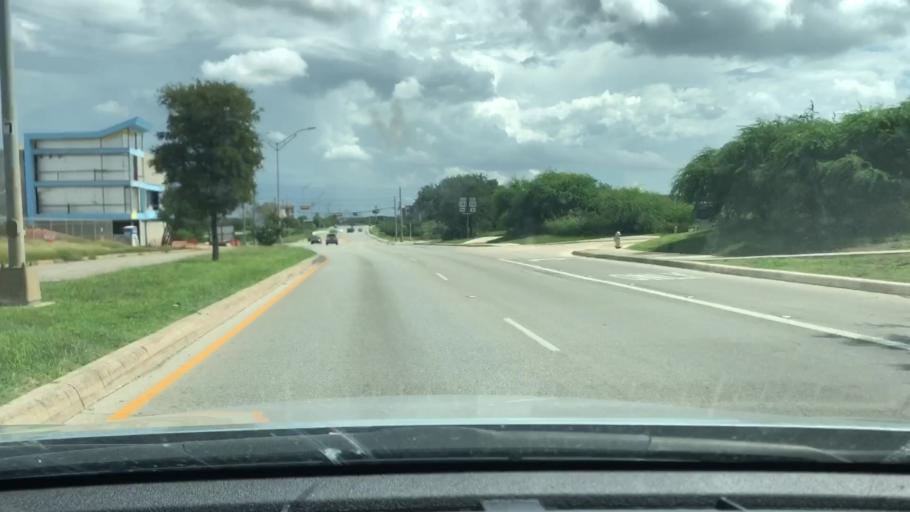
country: US
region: Texas
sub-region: Bexar County
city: Hollywood Park
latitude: 29.6149
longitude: -98.4702
